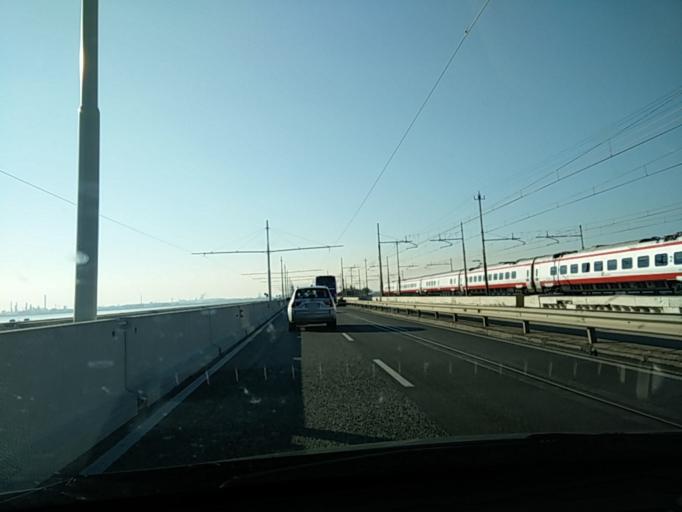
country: IT
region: Veneto
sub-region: Provincia di Venezia
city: Campalto
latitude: 45.4519
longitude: 12.3021
